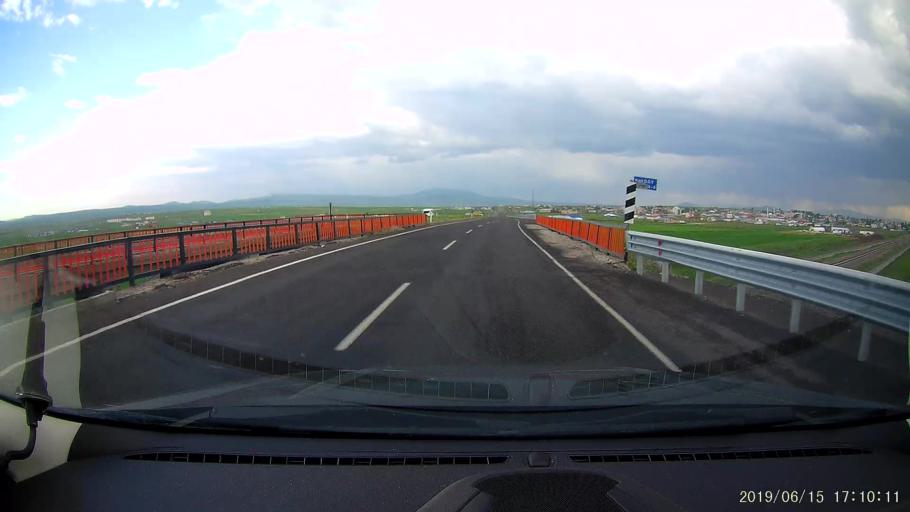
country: TR
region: Kars
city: Kars
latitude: 40.6250
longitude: 43.1339
